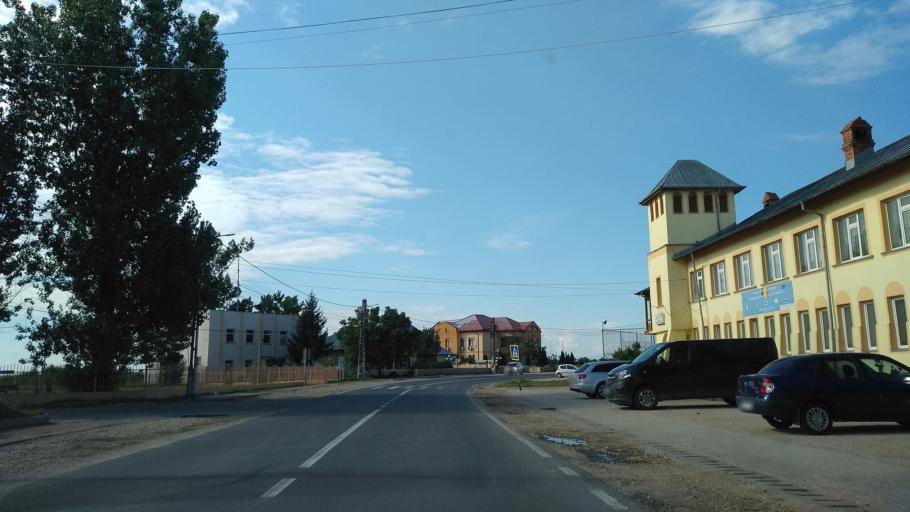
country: RO
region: Dambovita
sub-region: Comuna Petresti
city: Petresti
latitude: 44.6533
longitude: 25.3363
